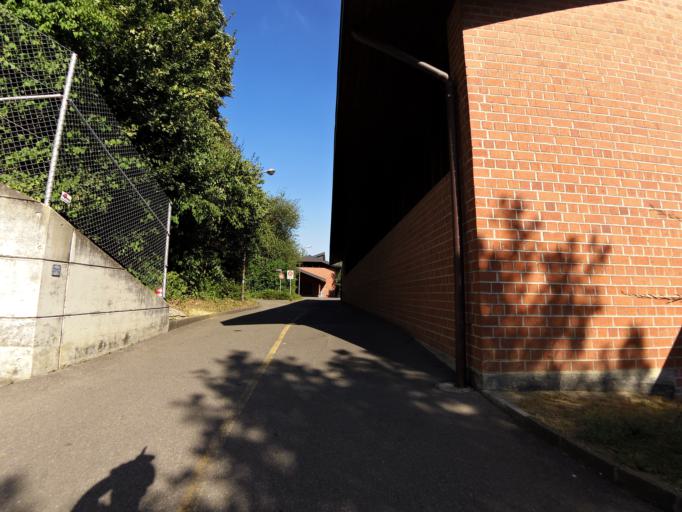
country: CH
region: Aargau
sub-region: Bezirk Lenzburg
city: Niederlenz
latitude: 47.4175
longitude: 8.1711
